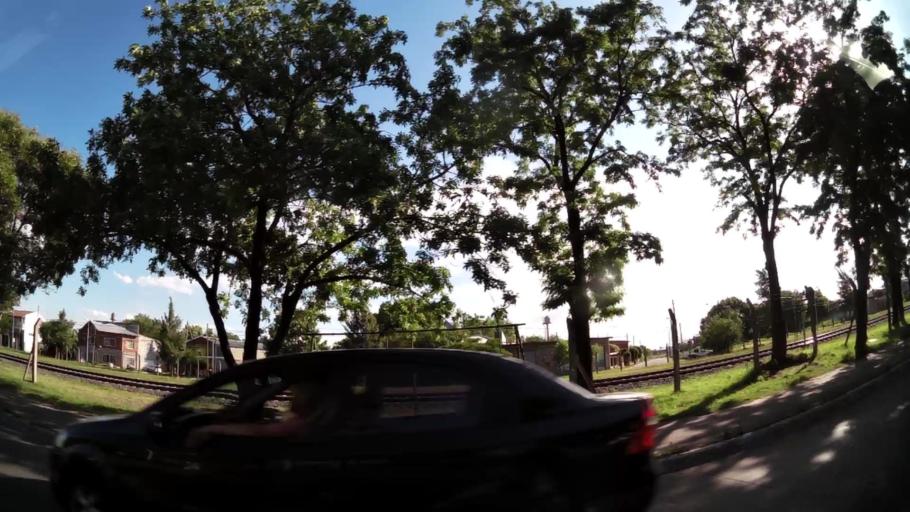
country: AR
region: Buenos Aires
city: Santa Catalina - Dique Lujan
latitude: -34.4918
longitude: -58.7103
